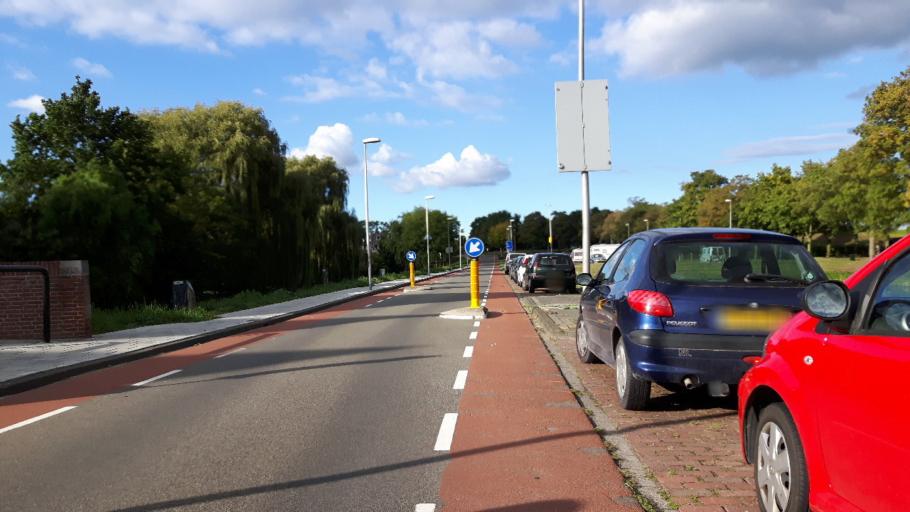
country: NL
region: Utrecht
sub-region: Gemeente Vianen
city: Vianen
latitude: 51.9940
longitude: 5.0960
